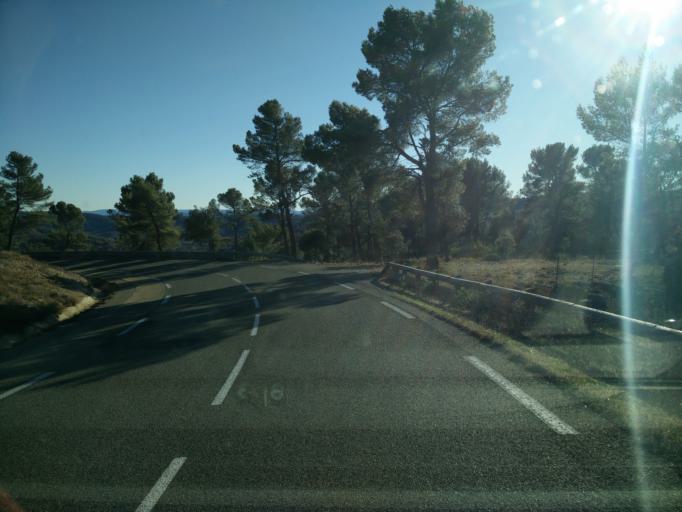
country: FR
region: Provence-Alpes-Cote d'Azur
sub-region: Departement du Var
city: Salernes
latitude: 43.5775
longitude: 6.2205
